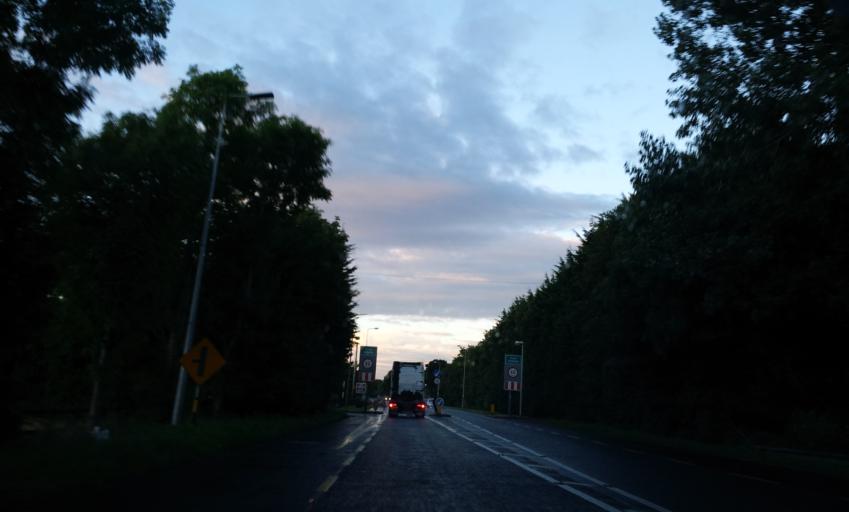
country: IE
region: Munster
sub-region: County Limerick
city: Rathkeale
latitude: 52.5322
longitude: -8.8767
